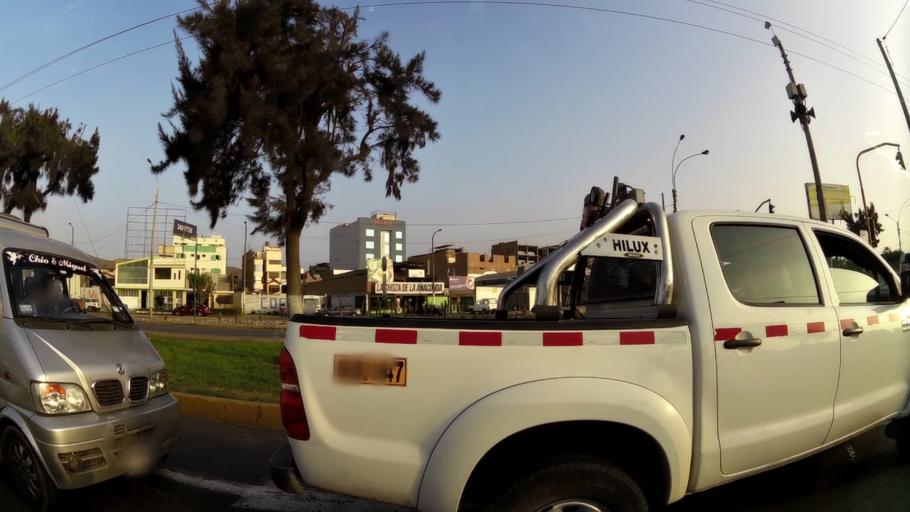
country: PE
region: Lima
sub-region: Lima
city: Independencia
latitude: -11.9913
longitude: -77.0816
